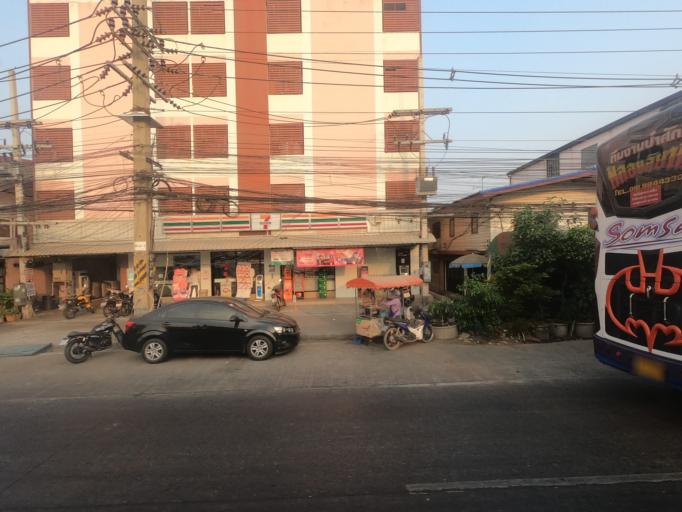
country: TH
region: Pathum Thani
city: Khlong Luang
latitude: 14.1336
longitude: 100.6187
